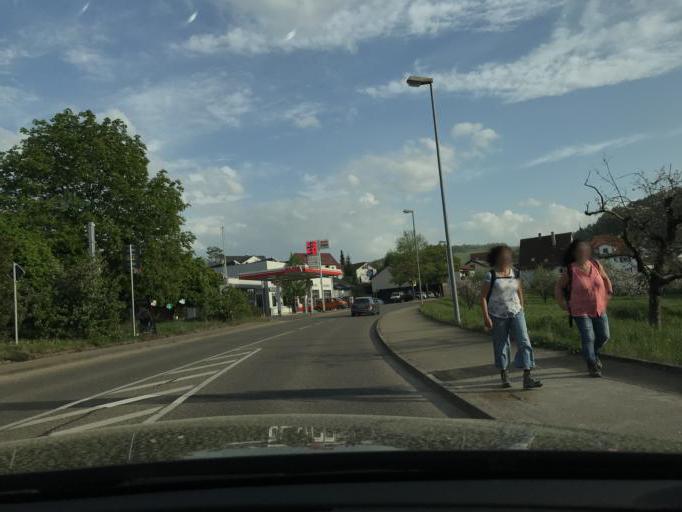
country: DE
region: Baden-Wuerttemberg
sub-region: Regierungsbezirk Stuttgart
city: Weinstadt-Endersbach
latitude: 48.7891
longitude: 9.3623
